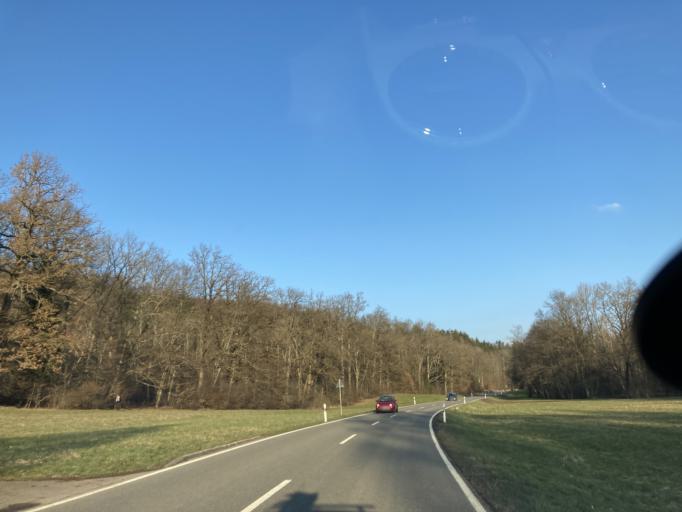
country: DE
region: Baden-Wuerttemberg
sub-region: Tuebingen Region
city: Bodelshausen
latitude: 48.4306
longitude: 8.9578
